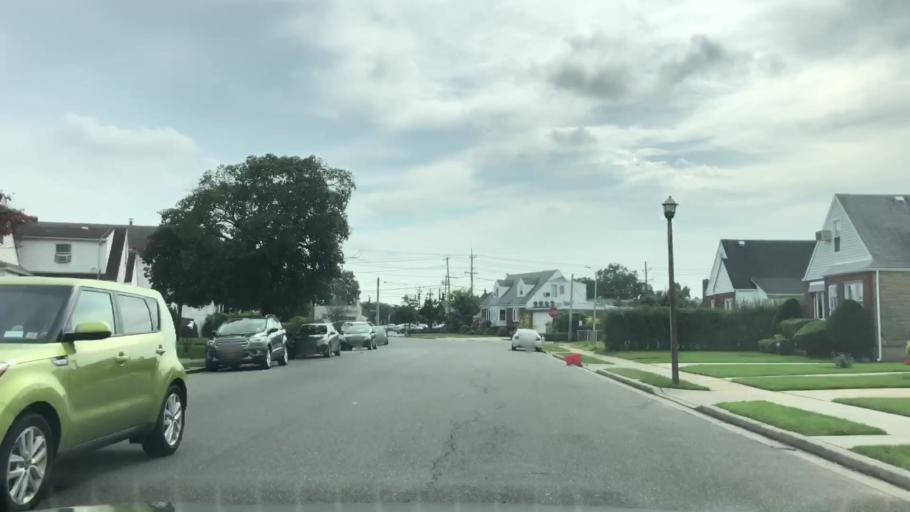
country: US
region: New York
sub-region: Nassau County
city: South Floral Park
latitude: 40.7084
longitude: -73.6943
